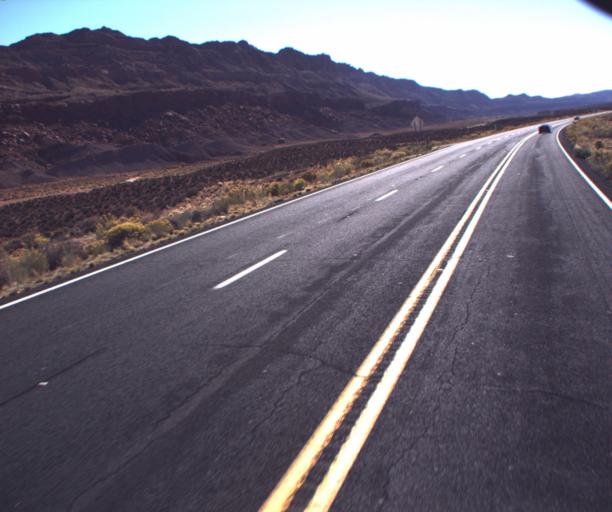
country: US
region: Arizona
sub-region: Coconino County
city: Tuba City
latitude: 36.2557
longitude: -111.4217
